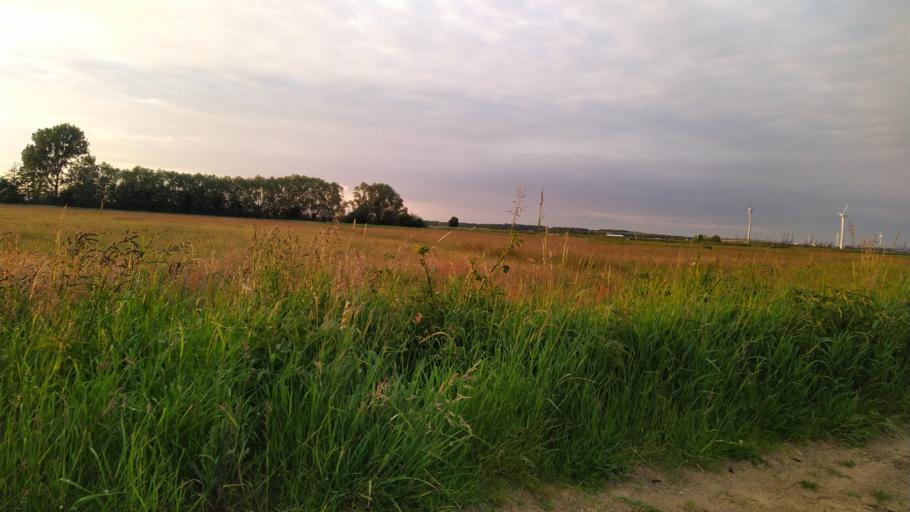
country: DE
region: Lower Saxony
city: Neu Wulmstorf
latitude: 53.4923
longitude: 9.8265
